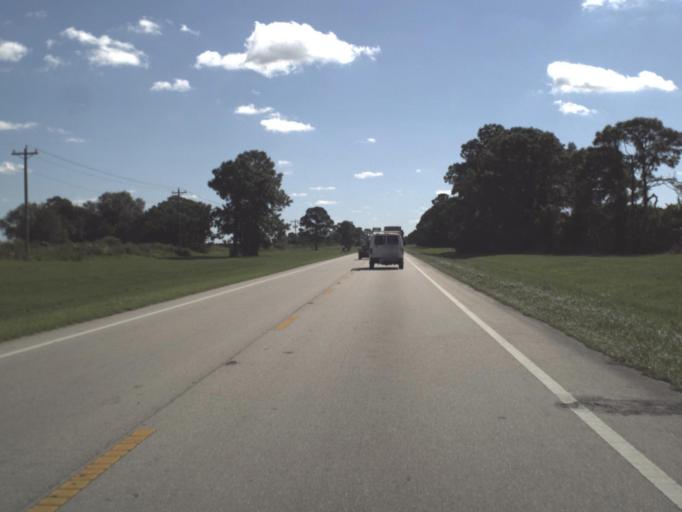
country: US
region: Florida
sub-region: Collier County
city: Immokalee
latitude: 26.5001
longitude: -81.4916
